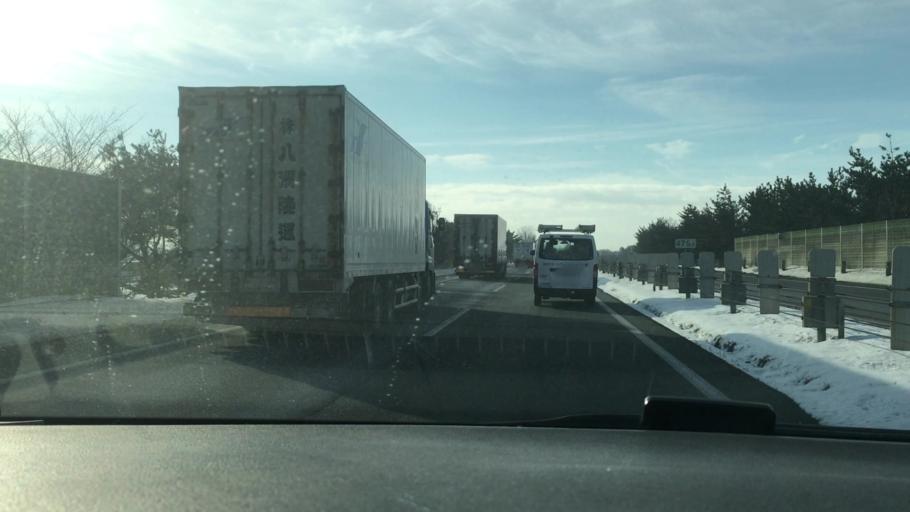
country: JP
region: Iwate
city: Hanamaki
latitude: 39.3963
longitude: 141.0926
